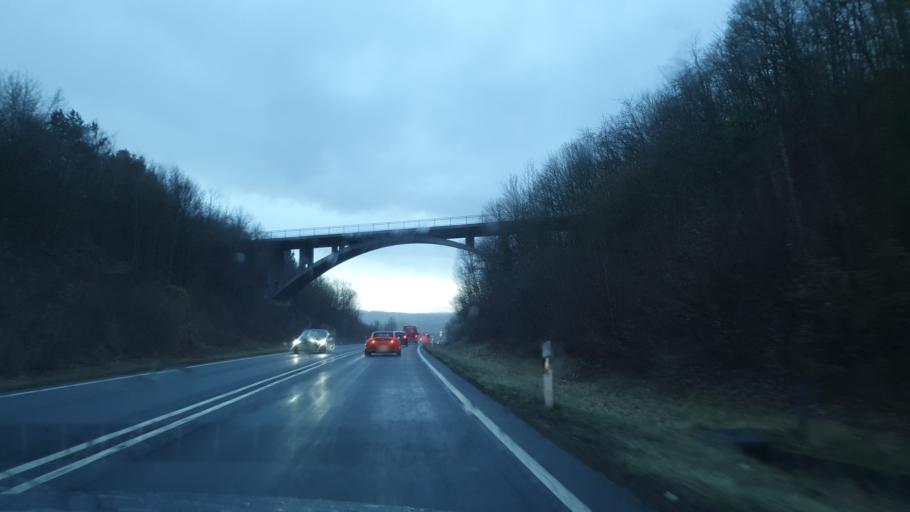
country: DE
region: Rheinland-Pfalz
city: Mendig
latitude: 50.3688
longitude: 7.2697
